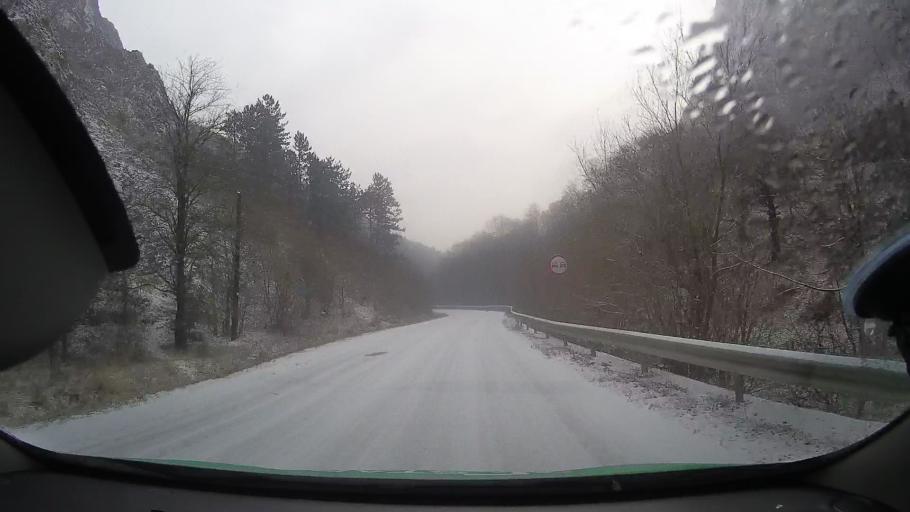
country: RO
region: Alba
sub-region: Comuna Livezile
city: Livezile
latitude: 46.3744
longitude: 23.5845
